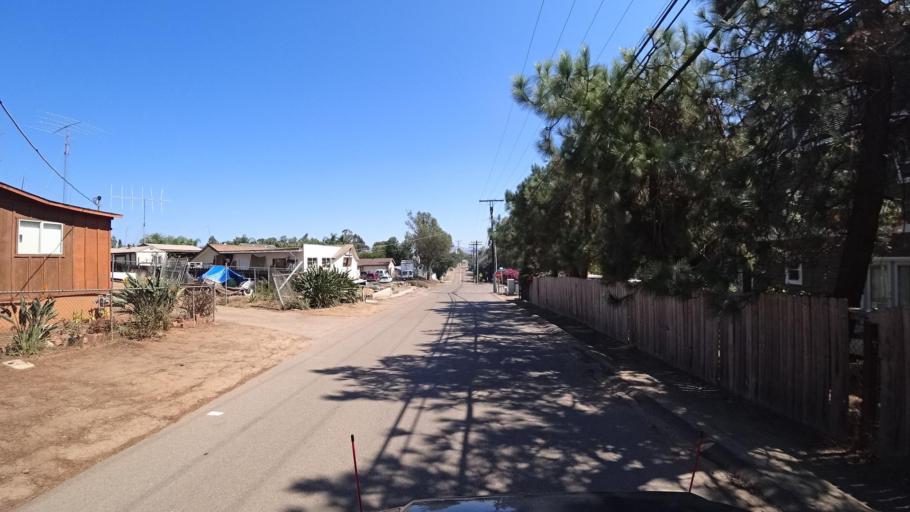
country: US
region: California
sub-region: San Diego County
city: Crest
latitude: 32.8059
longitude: -116.8667
